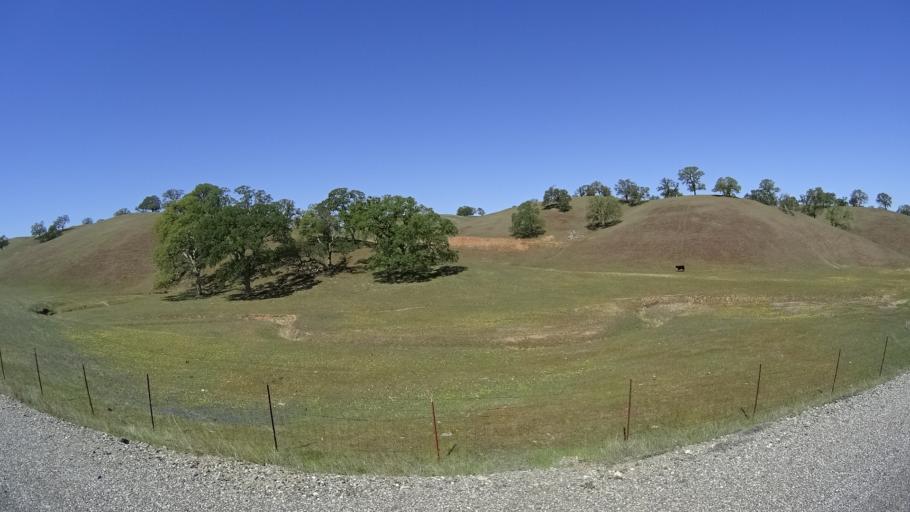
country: US
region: California
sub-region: Glenn County
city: Orland
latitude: 39.7439
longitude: -122.3743
